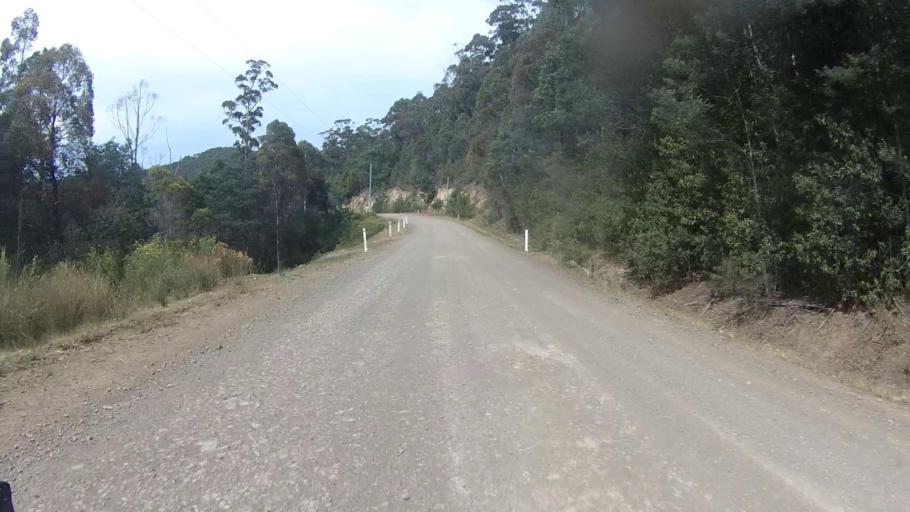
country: AU
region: Tasmania
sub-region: Sorell
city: Sorell
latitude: -42.7705
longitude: 147.8305
